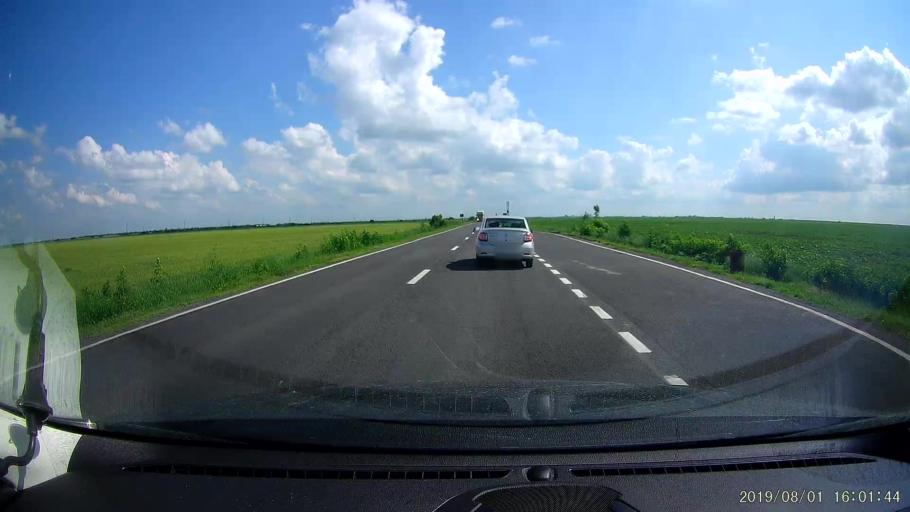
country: RO
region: Ialomita
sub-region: Comuna Ciulnita
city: Ciulnita
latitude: 44.5030
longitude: 27.3895
